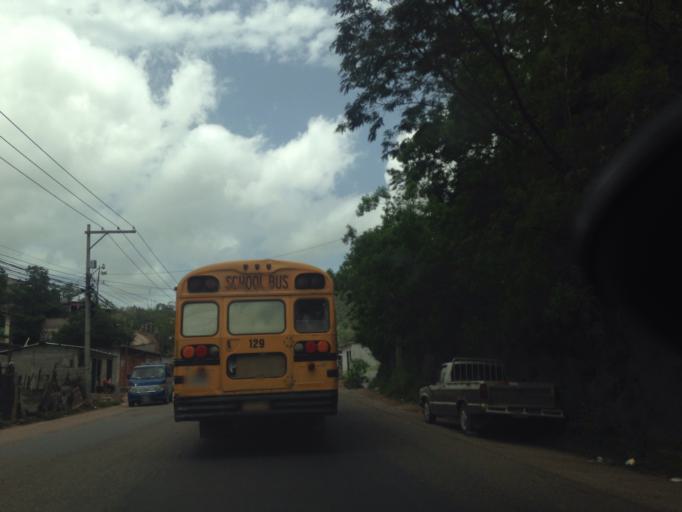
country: HN
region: Francisco Morazan
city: El Tablon
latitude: 14.0552
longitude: -87.1578
